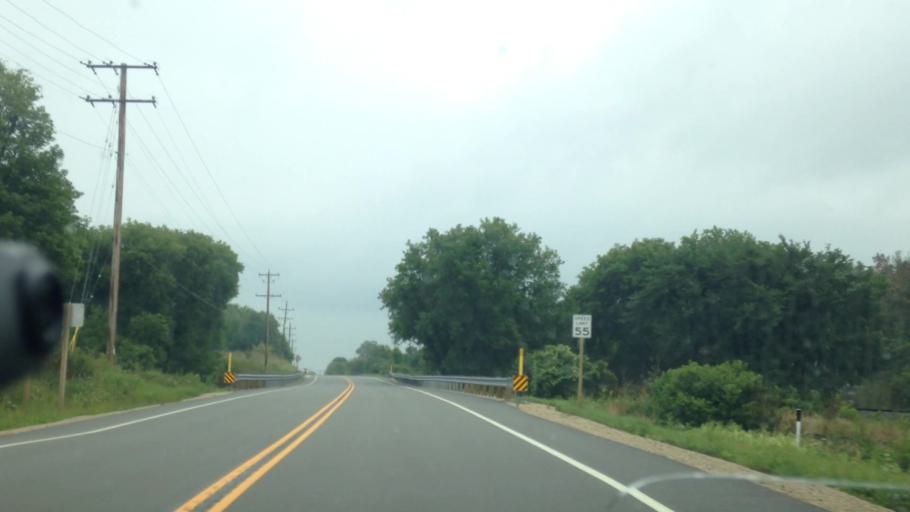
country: US
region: Wisconsin
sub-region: Washington County
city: Slinger
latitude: 43.3035
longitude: -88.2396
